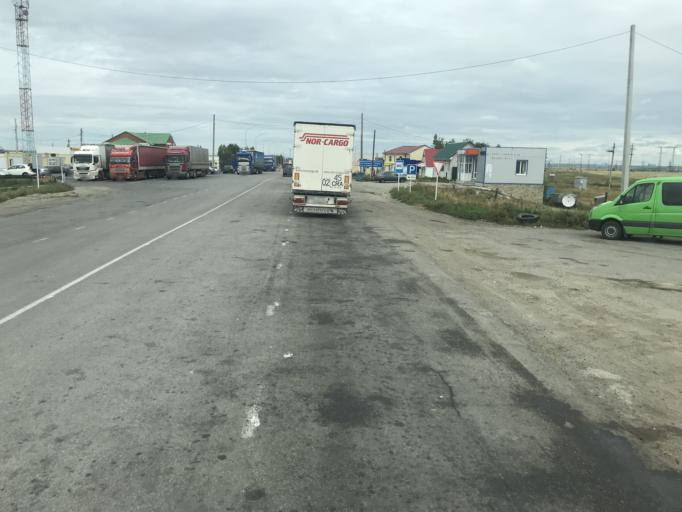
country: RU
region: Chelyabinsk
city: Bobrovka
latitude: 53.9979
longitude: 61.6432
